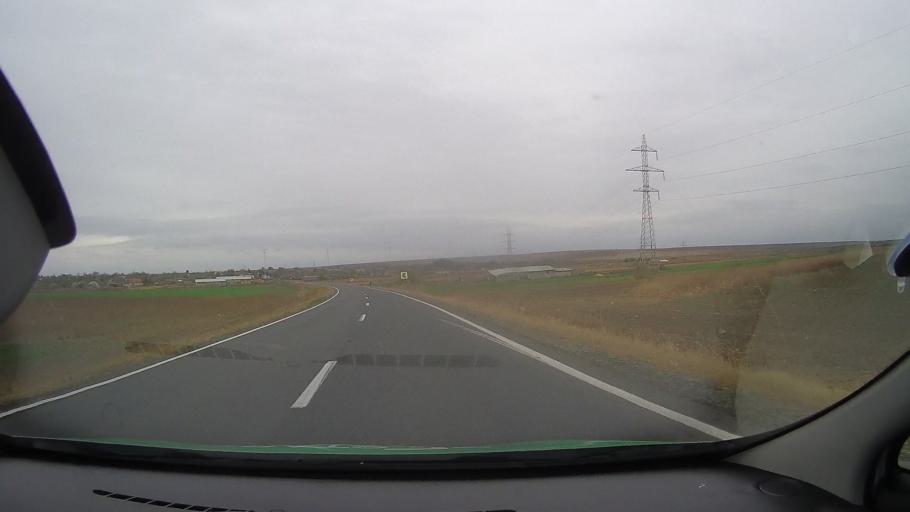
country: RO
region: Constanta
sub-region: Comuna Nicolae Balcescu
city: Dorobantu
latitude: 44.4151
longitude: 28.3166
